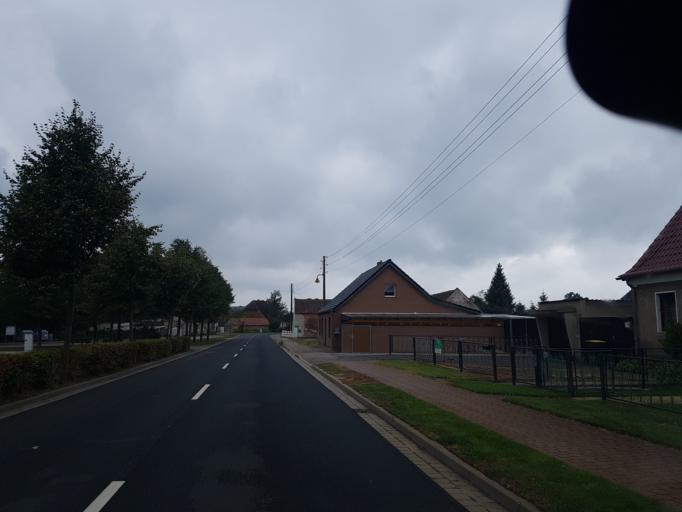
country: DE
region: Saxony-Anhalt
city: Tucheim
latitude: 52.3132
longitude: 12.1221
